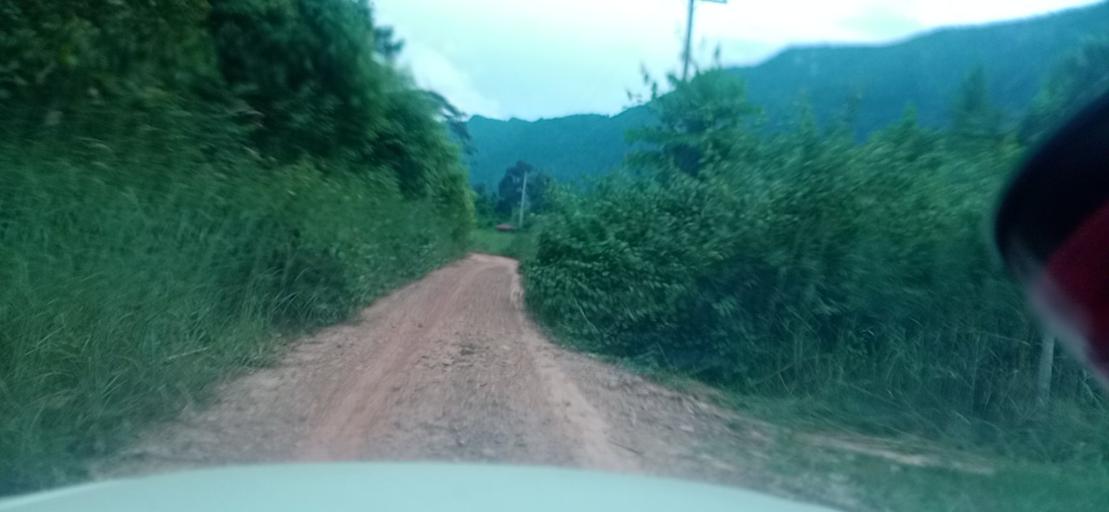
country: TH
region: Changwat Bueng Kan
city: Pak Khat
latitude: 18.5627
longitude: 103.2851
